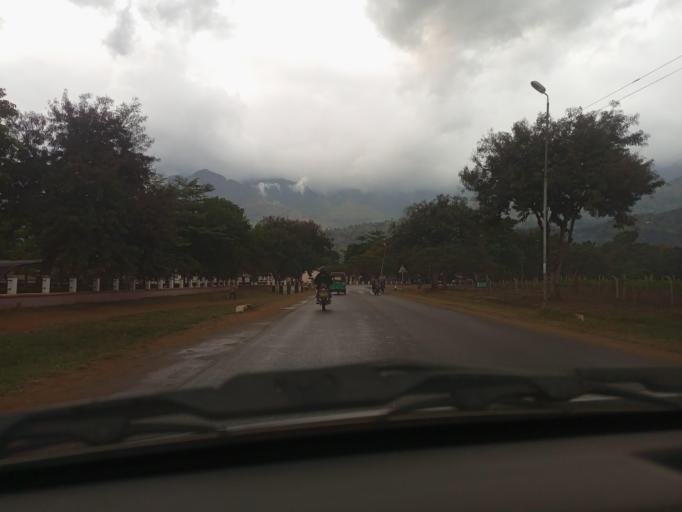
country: TZ
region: Morogoro
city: Morogoro
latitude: -6.8434
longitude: 37.6566
